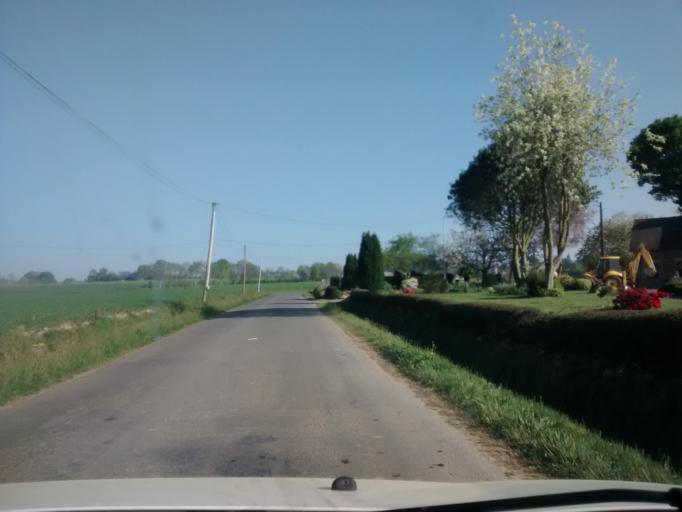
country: FR
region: Brittany
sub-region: Departement d'Ille-et-Vilaine
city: Saint-Sauveur-des-Landes
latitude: 48.3080
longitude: -1.3084
